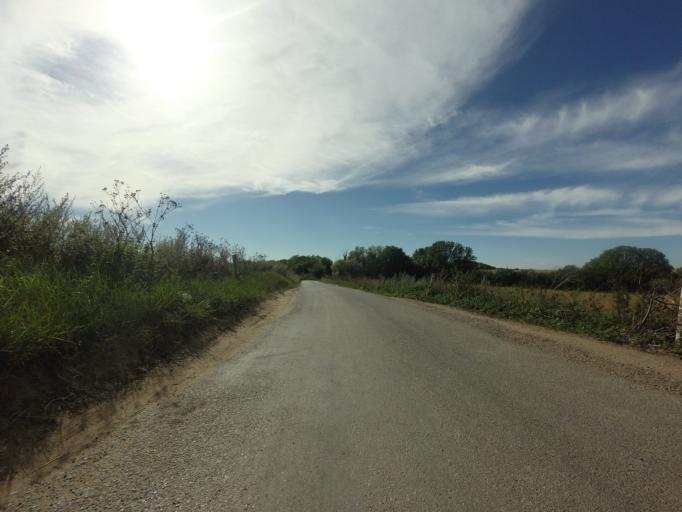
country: GB
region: England
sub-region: Kent
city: Herne Bay
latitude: 51.3673
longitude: 1.1916
